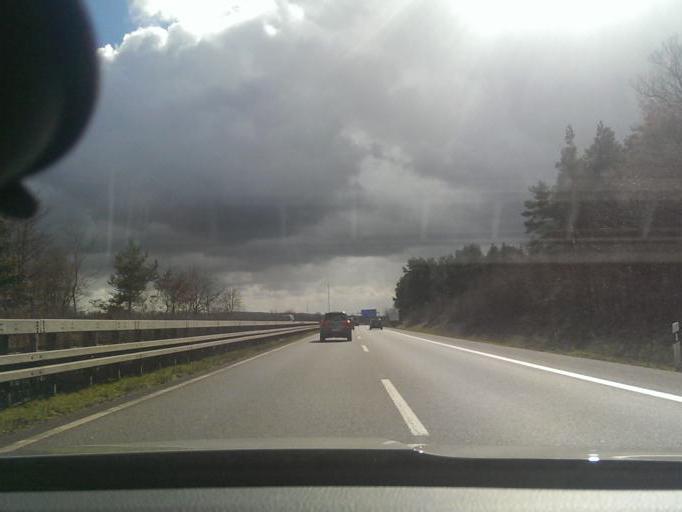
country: DE
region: Lower Saxony
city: Lehre
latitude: 52.3235
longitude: 10.7329
